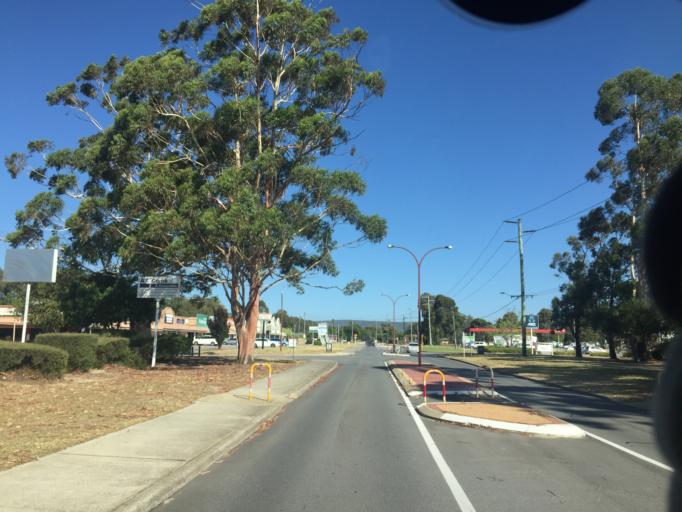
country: AU
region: Western Australia
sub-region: Gosnells
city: Maddington
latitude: -32.0519
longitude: 115.9793
